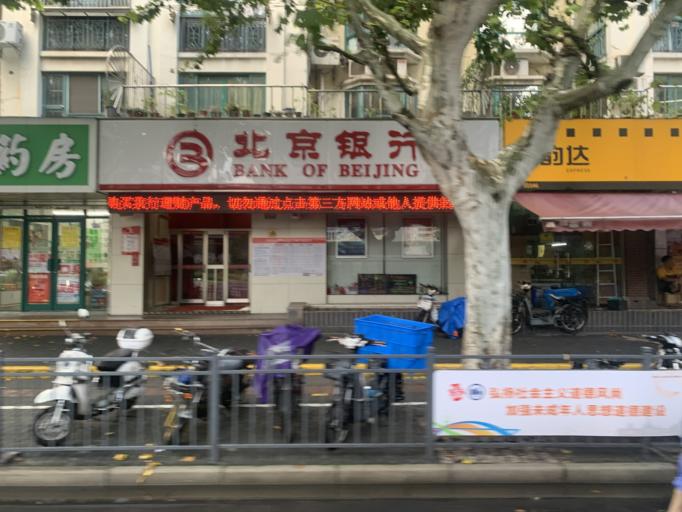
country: CN
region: Shanghai Shi
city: Luwan
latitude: 31.2141
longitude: 121.4715
